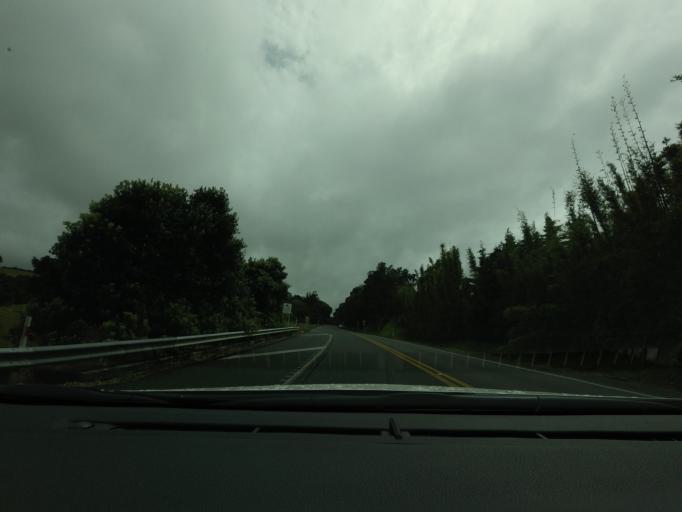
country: NZ
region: Auckland
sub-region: Auckland
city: Warkworth
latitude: -36.5543
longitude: 174.7074
